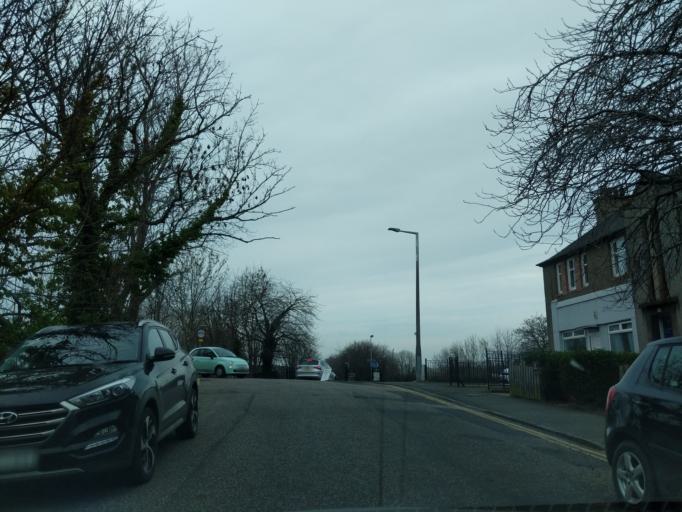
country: GB
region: Scotland
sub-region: Edinburgh
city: Edinburgh
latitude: 55.9686
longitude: -3.1953
